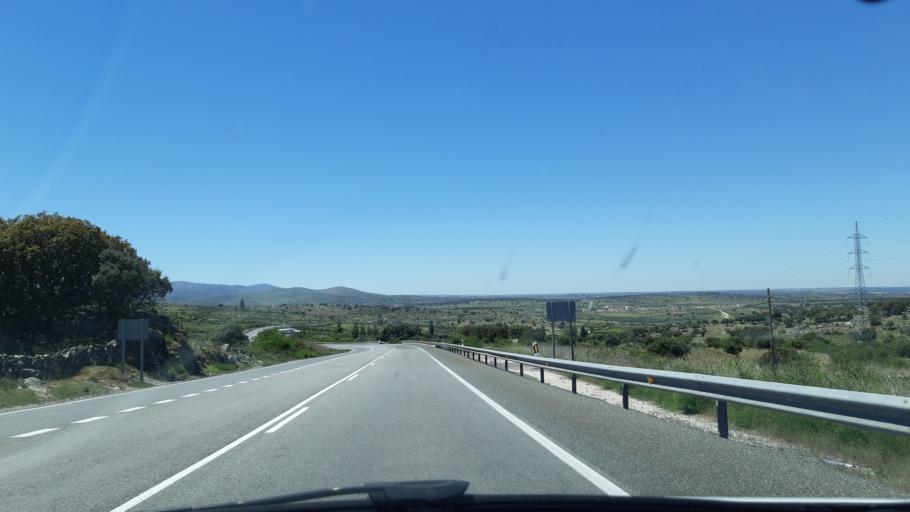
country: ES
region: Castille and Leon
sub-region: Provincia de Segovia
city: Vegas de Matute
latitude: 40.7502
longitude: -4.2903
